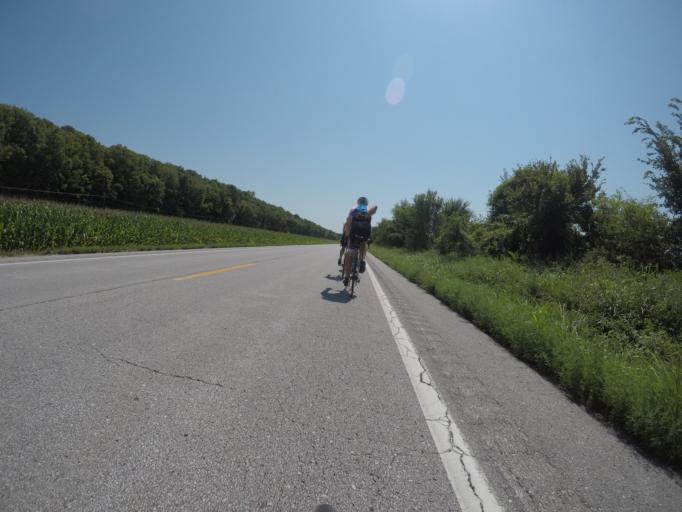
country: US
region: Kansas
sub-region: Leavenworth County
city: Leavenworth
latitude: 39.3324
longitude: -94.8589
